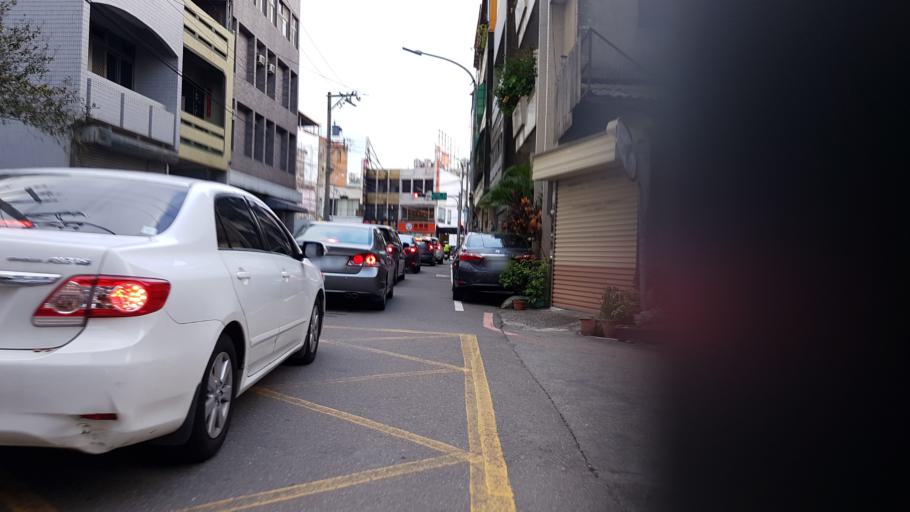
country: TW
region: Taiwan
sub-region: Hsinchu
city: Hsinchu
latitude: 24.7875
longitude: 121.0110
